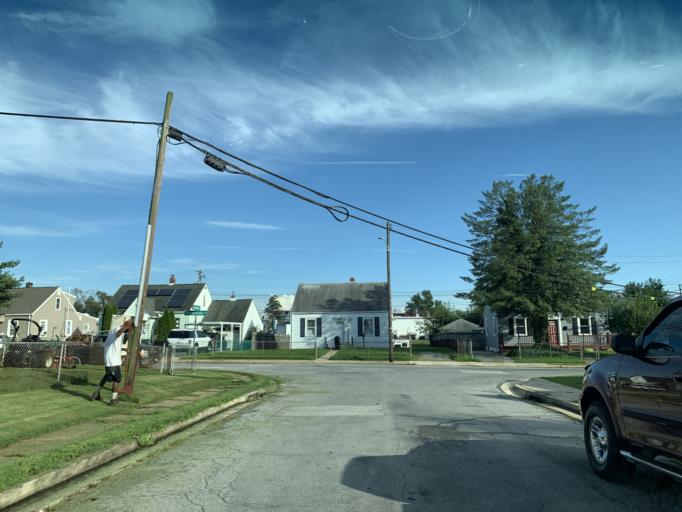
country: US
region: Maryland
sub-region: Baltimore County
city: Essex
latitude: 39.3058
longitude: -76.4846
